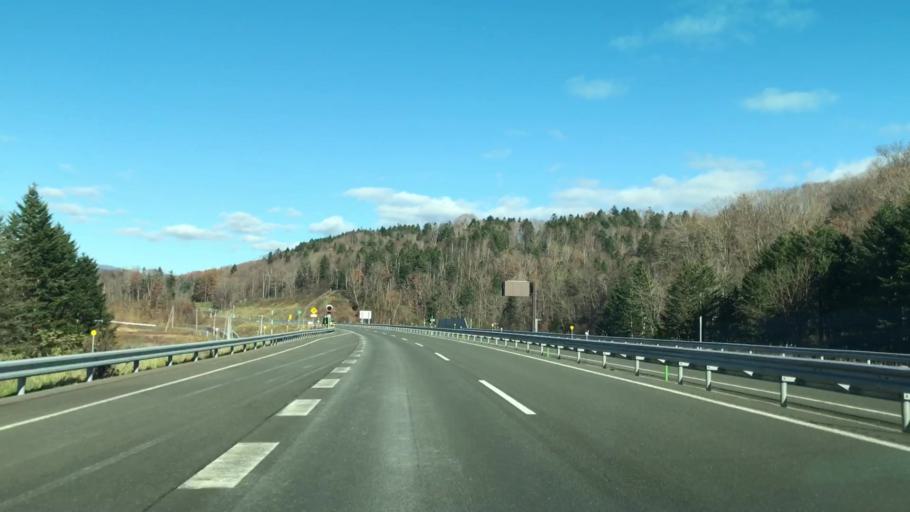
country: JP
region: Hokkaido
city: Shimo-furano
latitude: 42.9215
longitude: 142.2000
